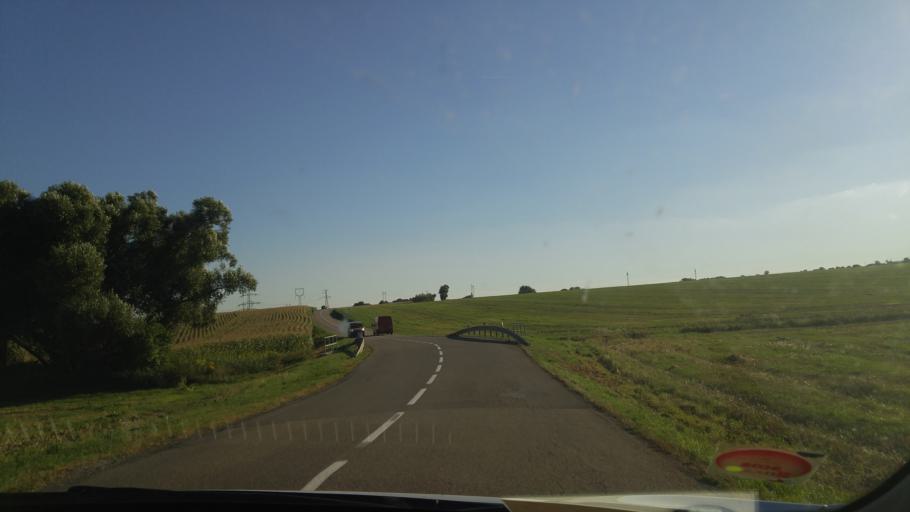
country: CZ
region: South Moravian
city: Ricany
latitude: 49.2263
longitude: 16.4173
